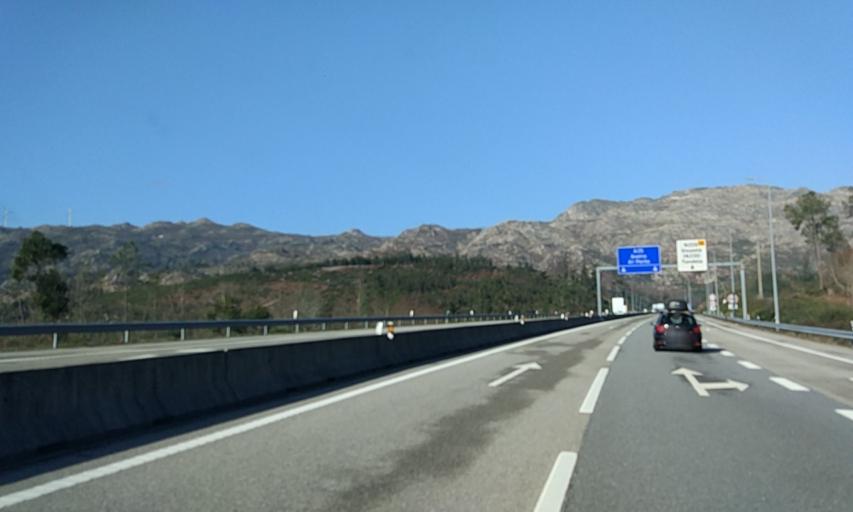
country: PT
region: Viseu
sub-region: Vouzela
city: Vouzela
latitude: 40.6507
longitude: -8.0656
